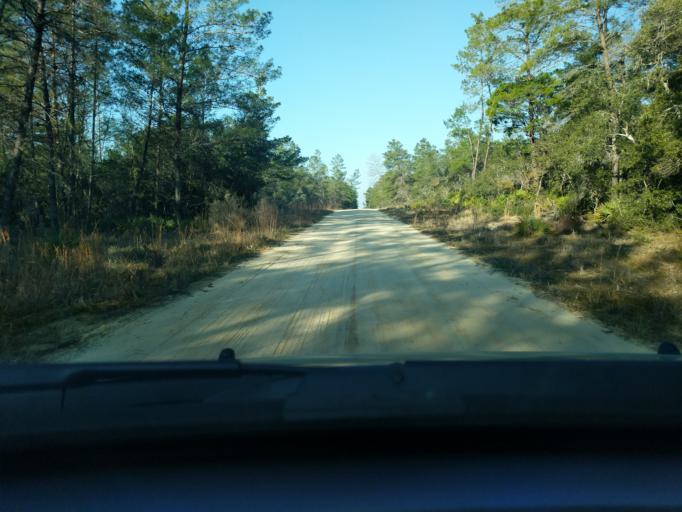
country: US
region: Florida
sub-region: Marion County
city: Silver Springs Shores
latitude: 29.2263
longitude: -81.7917
